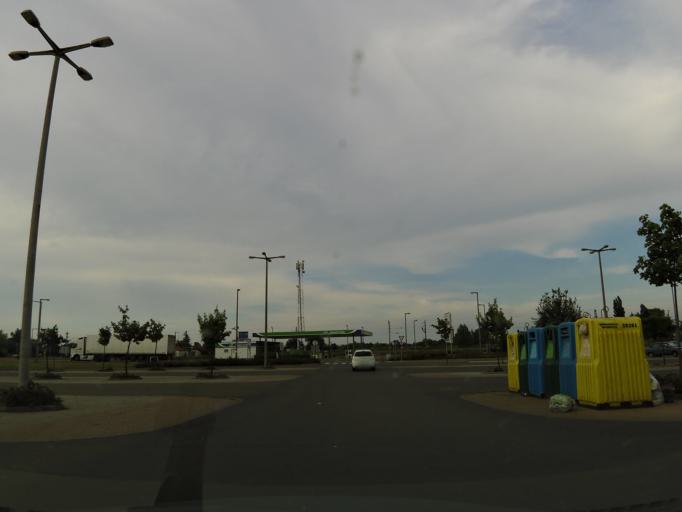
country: HU
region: Bacs-Kiskun
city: Kiskunhalas
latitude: 46.4190
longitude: 19.4980
